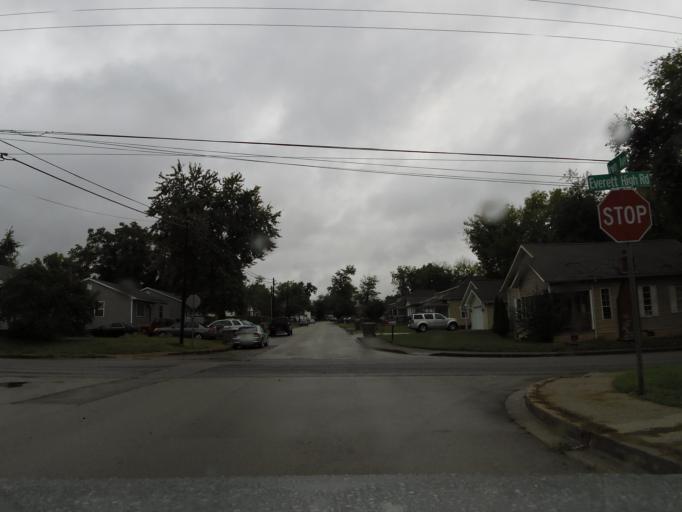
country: US
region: Tennessee
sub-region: Blount County
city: Maryville
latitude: 35.7711
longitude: -83.9608
